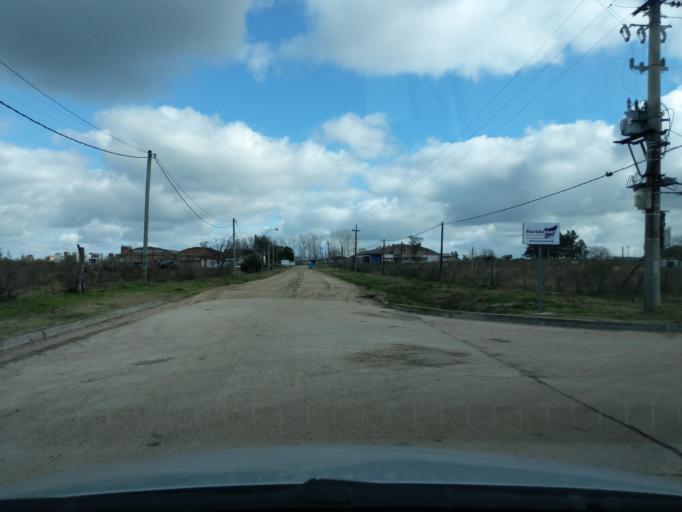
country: UY
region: Florida
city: Florida
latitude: -34.1097
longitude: -56.2209
